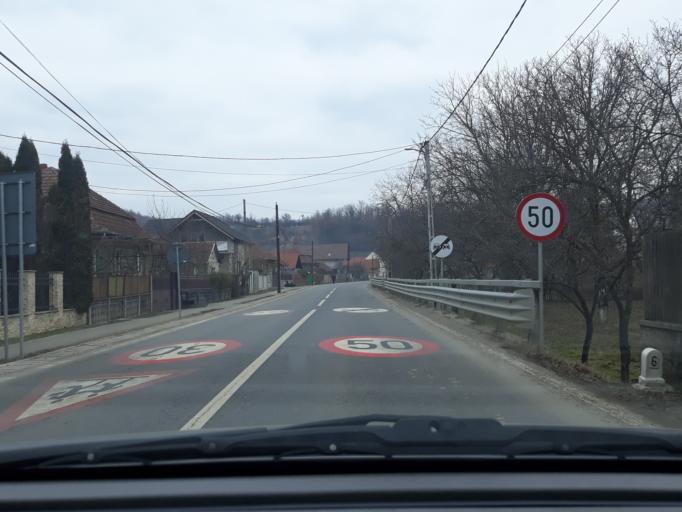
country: RO
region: Bihor
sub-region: Oras Alesd
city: Pestis
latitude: 47.0693
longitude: 22.4088
